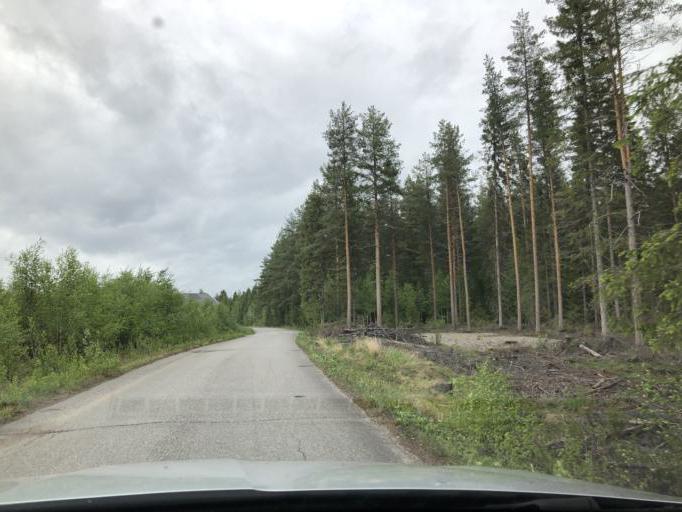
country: SE
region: Norrbotten
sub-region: Pitea Kommun
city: Roknas
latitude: 65.3899
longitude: 21.2696
